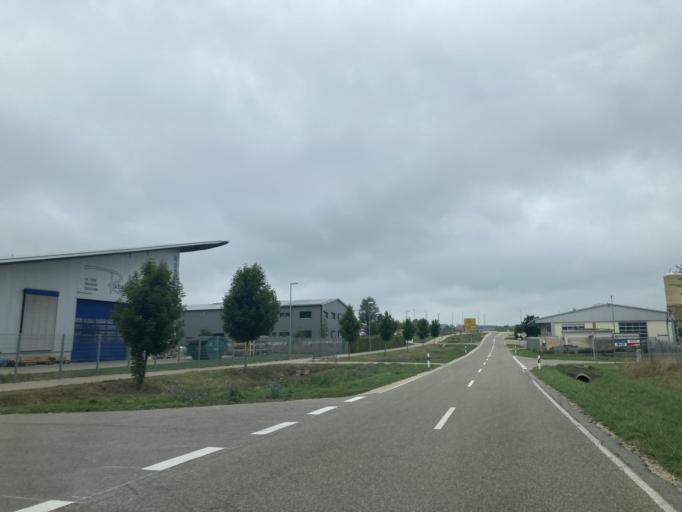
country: DE
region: Bavaria
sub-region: Swabia
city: Bachhagel
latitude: 48.6314
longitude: 10.3130
